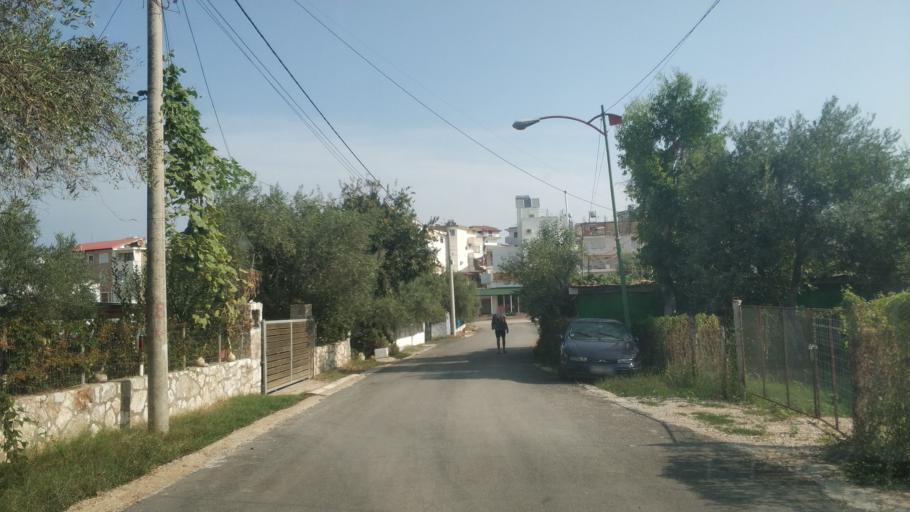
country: AL
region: Vlore
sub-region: Rrethi i Sarandes
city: Xarre
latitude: 39.7672
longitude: 19.9991
